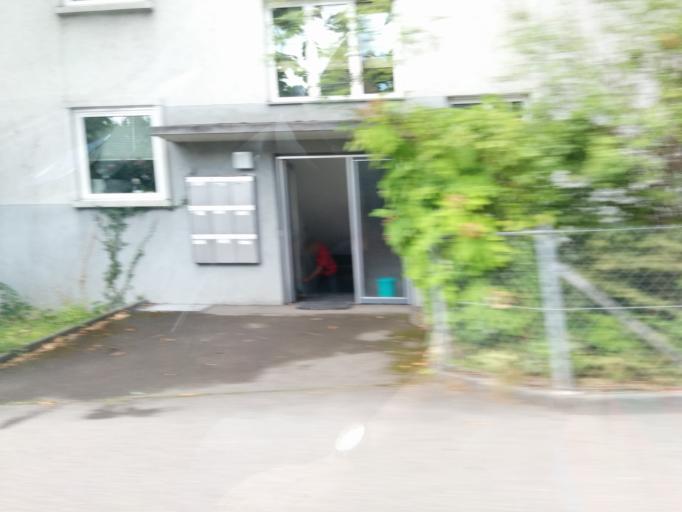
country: CH
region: Zurich
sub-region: Bezirk Meilen
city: Kuesnacht
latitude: 47.3199
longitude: 8.5844
